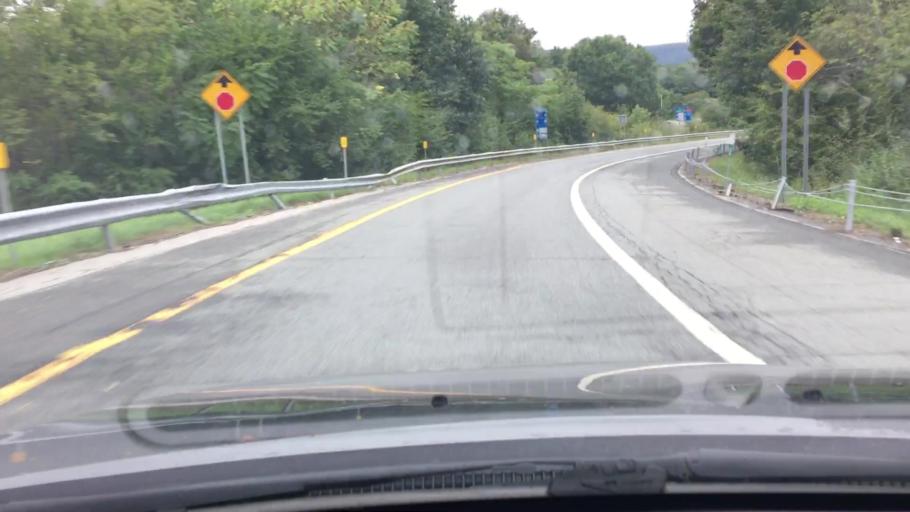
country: US
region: New York
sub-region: Orange County
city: Port Jervis
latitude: 41.3542
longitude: -74.6772
